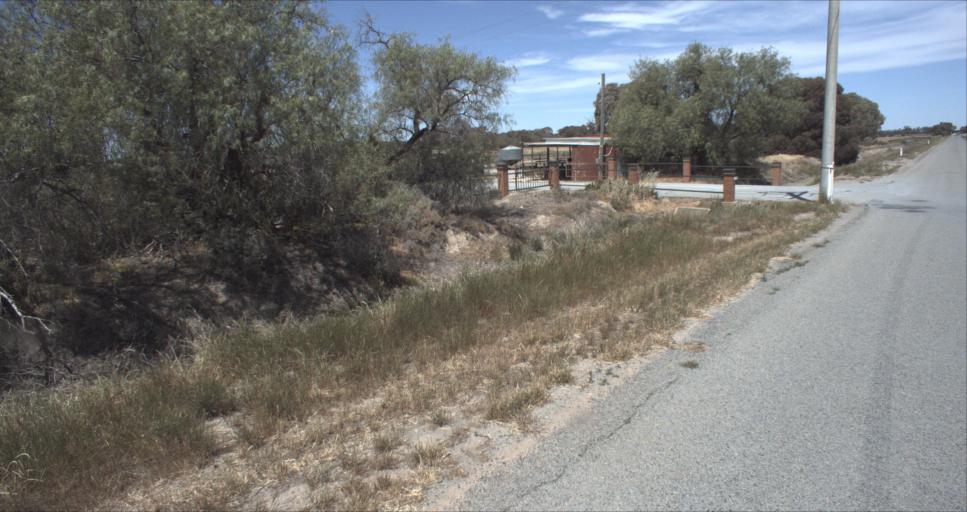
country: AU
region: New South Wales
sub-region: Leeton
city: Leeton
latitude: -34.5965
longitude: 146.4164
